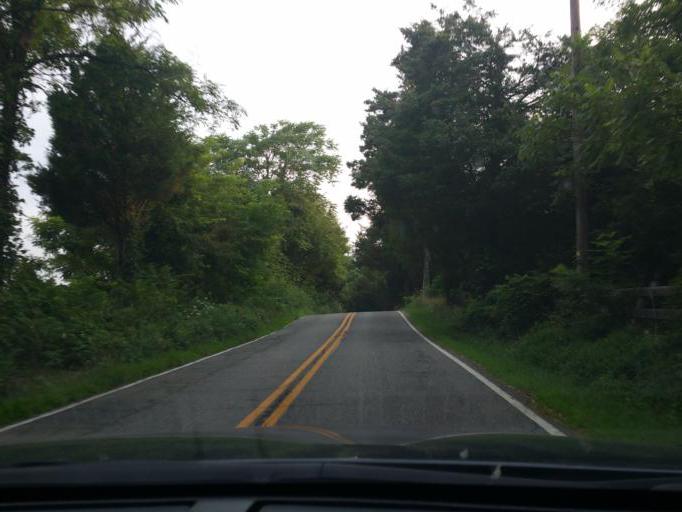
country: US
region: Maryland
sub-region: Cecil County
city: Rising Sun
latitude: 39.7193
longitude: -76.2007
